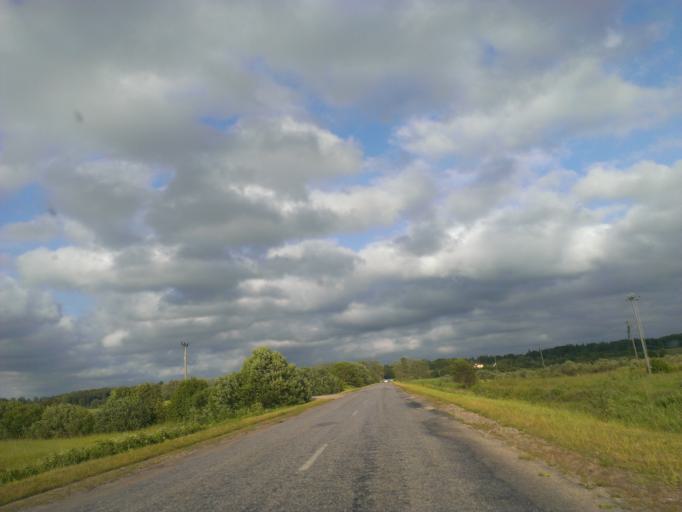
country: LV
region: Aizpute
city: Aizpute
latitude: 56.7319
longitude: 21.7122
